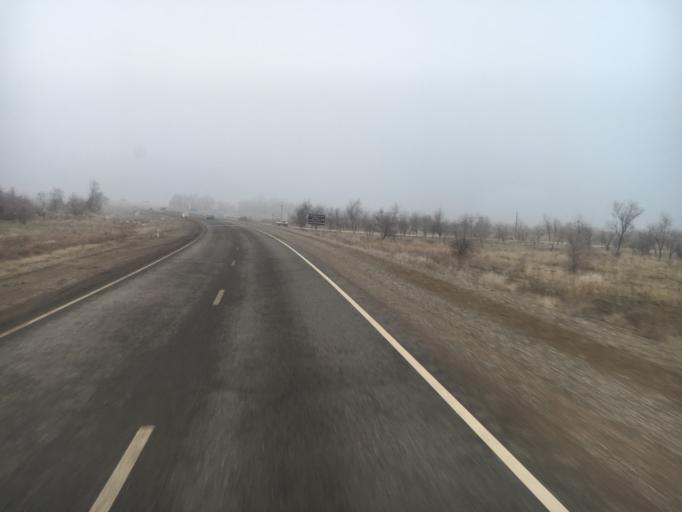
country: KZ
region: Zhambyl
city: Sarykemer
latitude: 43.0397
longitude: 71.5402
